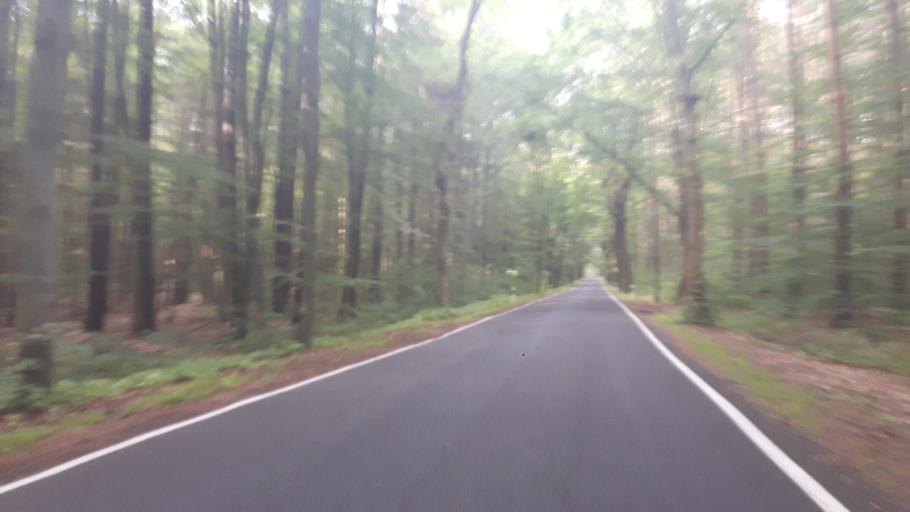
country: DE
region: Brandenburg
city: Hohenfinow
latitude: 52.7859
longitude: 13.8983
